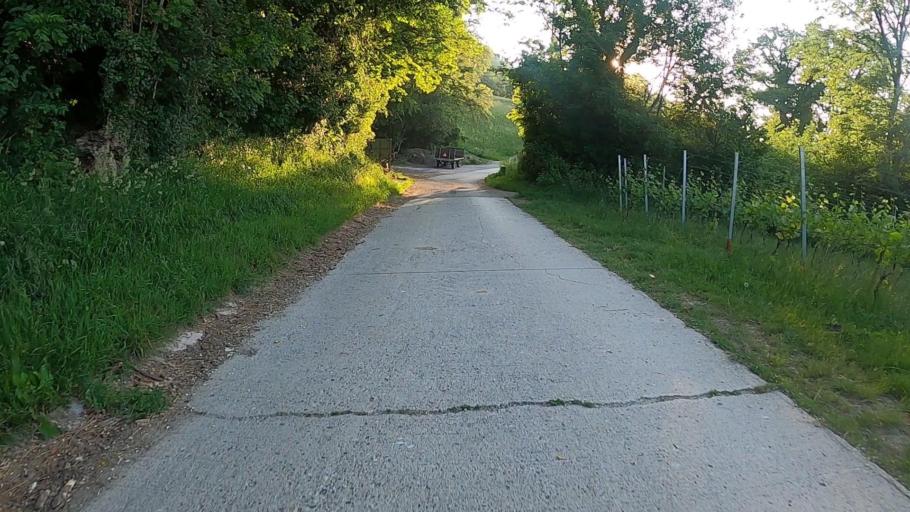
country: CH
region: Vaud
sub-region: Nyon District
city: Rolle
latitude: 46.4772
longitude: 6.3402
